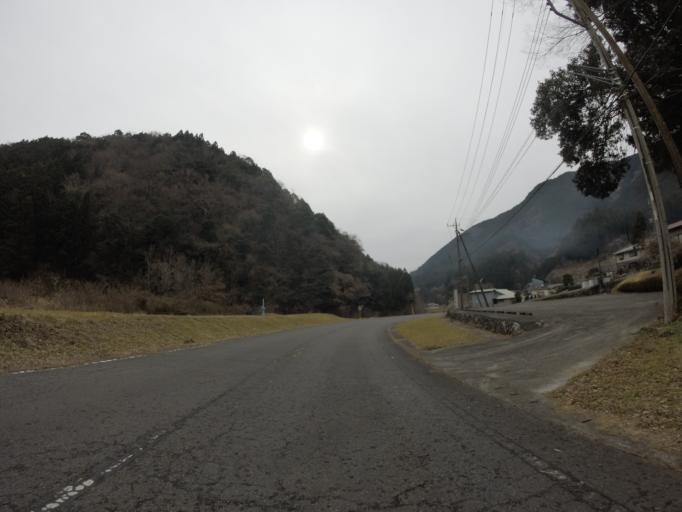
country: JP
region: Shizuoka
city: Fujinomiya
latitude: 35.2650
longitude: 138.5308
